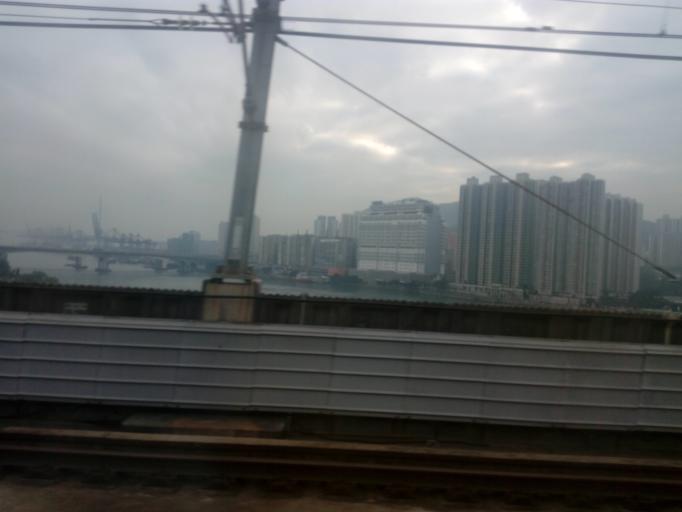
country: HK
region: Tsuen Wan
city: Tsuen Wan
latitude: 22.3567
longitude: 114.1132
